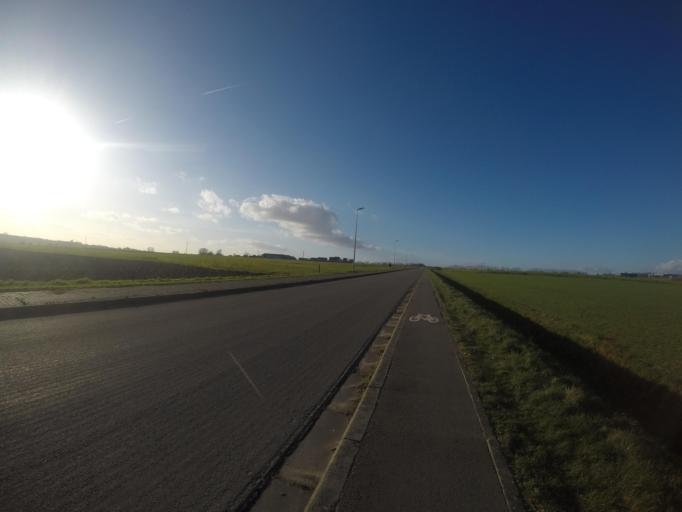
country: BE
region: Wallonia
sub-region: Province du Brabant Wallon
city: Tubize
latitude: 50.6946
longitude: 4.1803
